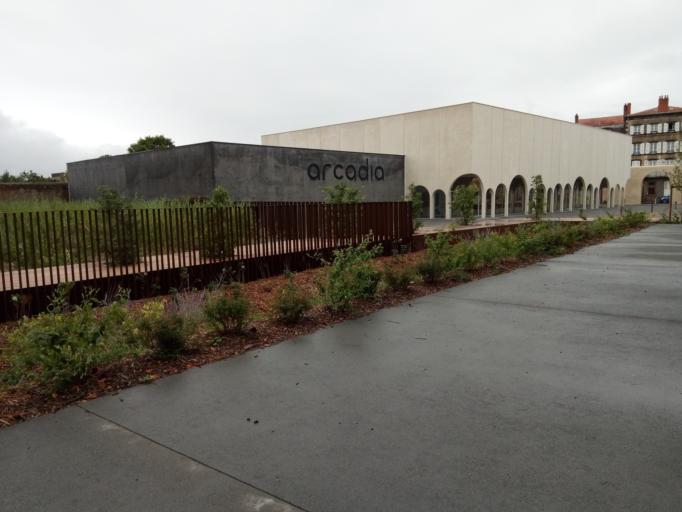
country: FR
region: Auvergne
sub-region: Departement du Puy-de-Dome
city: Riom
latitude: 45.8955
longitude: 3.1202
